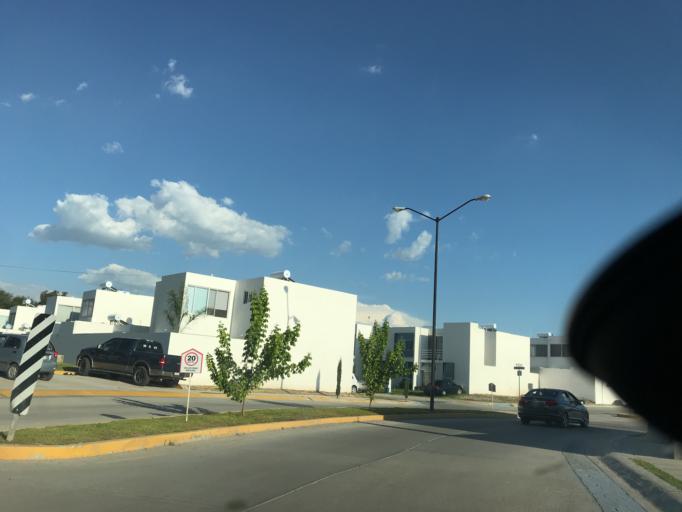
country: MX
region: Aguascalientes
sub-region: Aguascalientes
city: Pocitos
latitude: 21.8979
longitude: -102.3299
